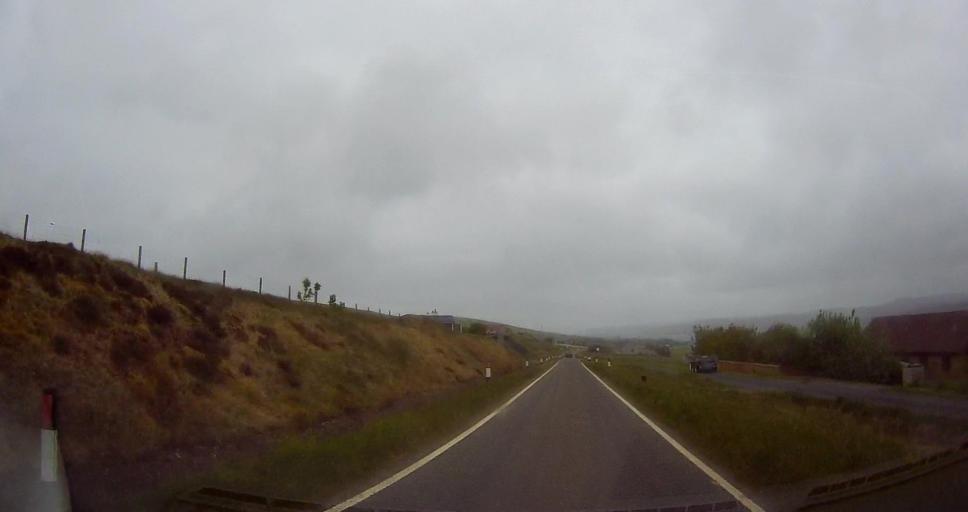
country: GB
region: Scotland
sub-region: Shetland Islands
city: Lerwick
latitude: 60.2764
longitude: -1.3900
